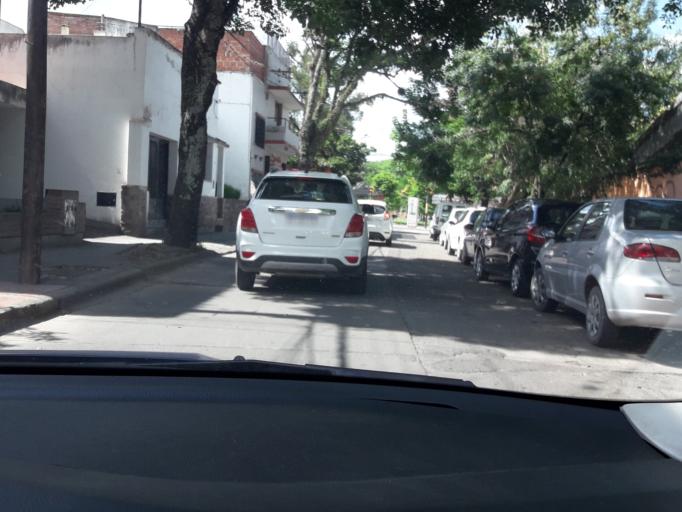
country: AR
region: Jujuy
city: San Salvador de Jujuy
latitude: -24.1850
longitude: -65.3135
